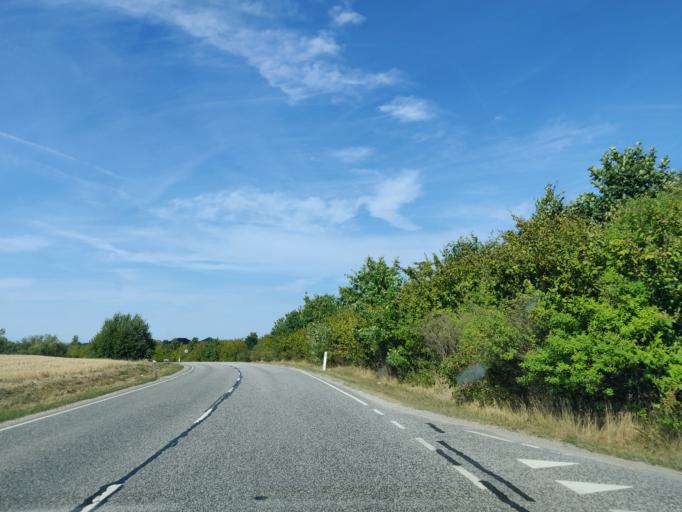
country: DK
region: Zealand
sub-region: Roskilde Kommune
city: Svogerslev
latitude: 55.6306
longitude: 12.0428
